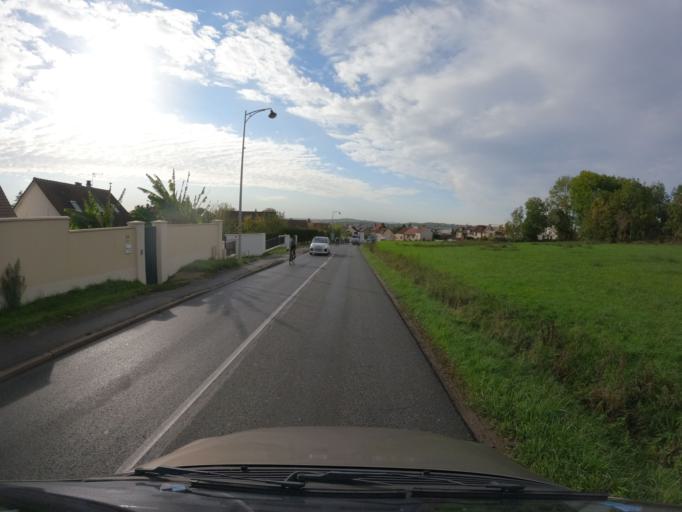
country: FR
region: Ile-de-France
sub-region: Departement de Seine-et-Marne
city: Courtry
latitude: 48.9206
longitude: 2.6039
